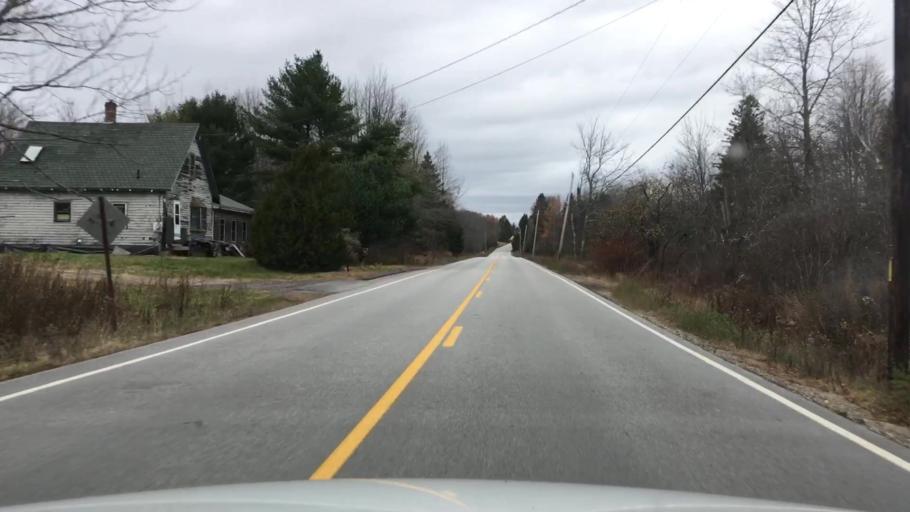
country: US
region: Maine
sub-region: Hancock County
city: Penobscot
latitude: 44.4696
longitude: -68.6362
